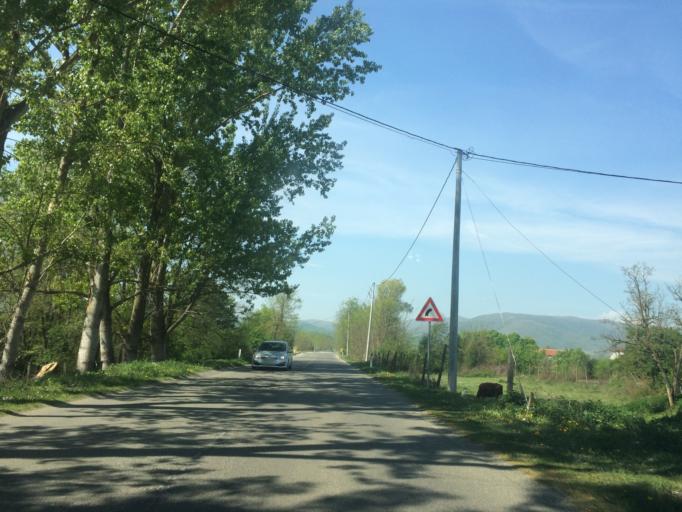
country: XK
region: Gjakova
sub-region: Komuna e Gjakoves
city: Gjakove
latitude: 42.3703
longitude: 20.3622
